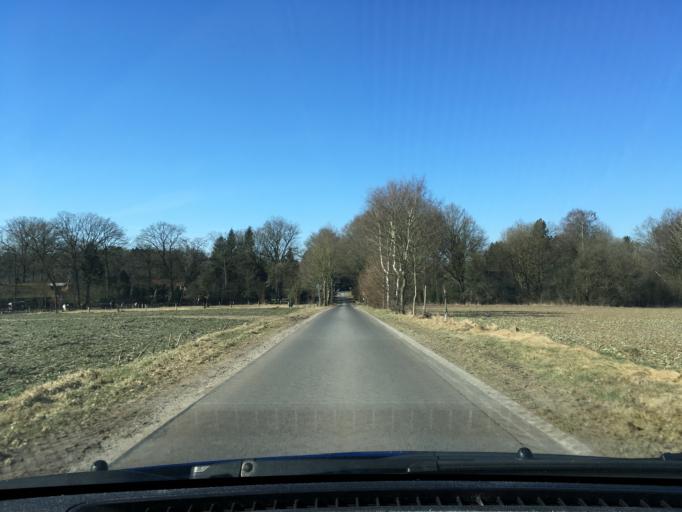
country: DE
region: Lower Saxony
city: Schneverdingen
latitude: 53.0829
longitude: 9.7716
